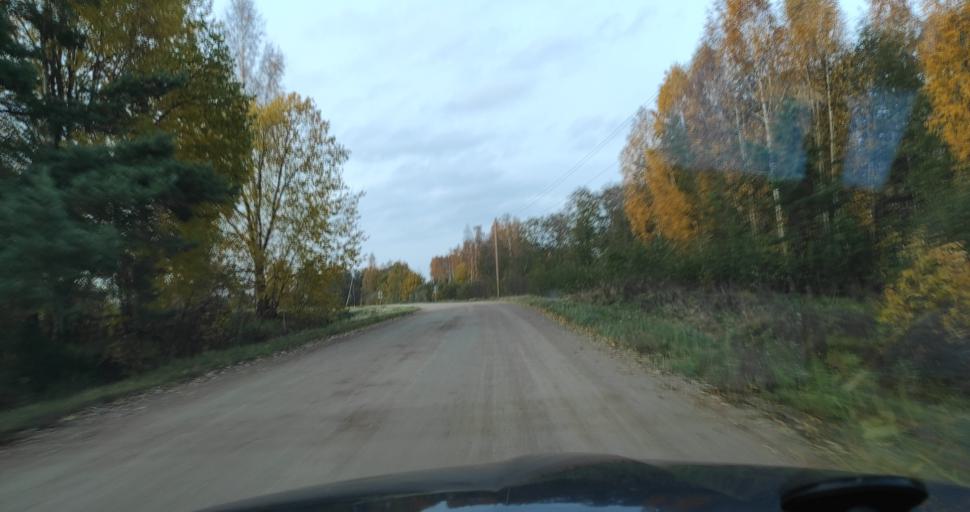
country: LV
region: Aizpute
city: Aizpute
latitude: 56.6619
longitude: 21.7962
